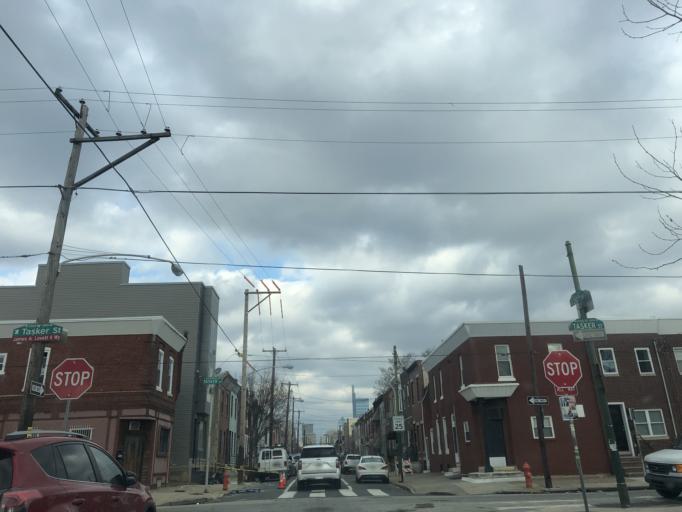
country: US
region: Pennsylvania
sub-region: Philadelphia County
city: Philadelphia
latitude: 39.9315
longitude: -75.1779
